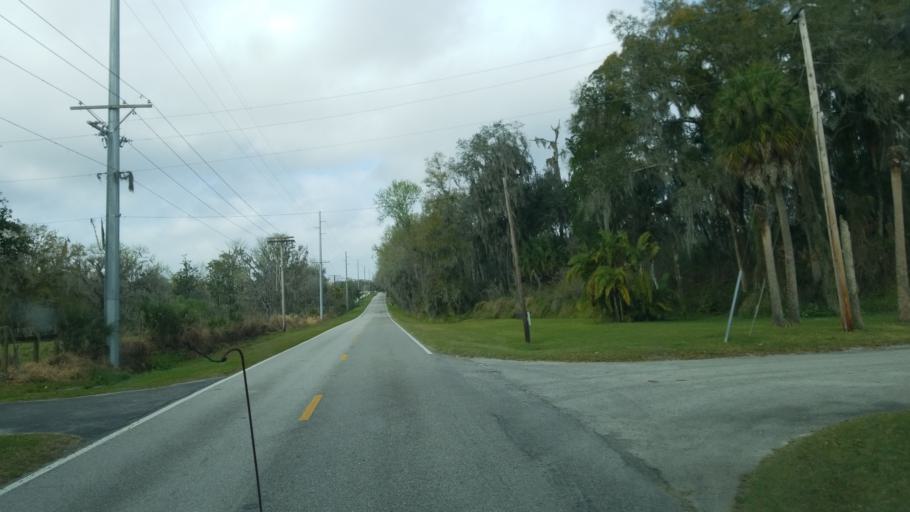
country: US
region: Florida
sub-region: Hillsborough County
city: Fish Hawk
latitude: 27.8866
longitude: -82.1179
